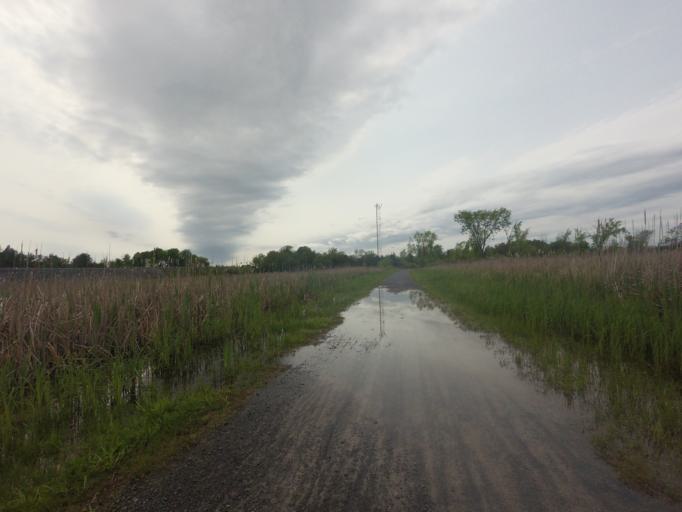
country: CA
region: Ontario
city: Kingston
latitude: 44.2803
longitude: -76.5612
